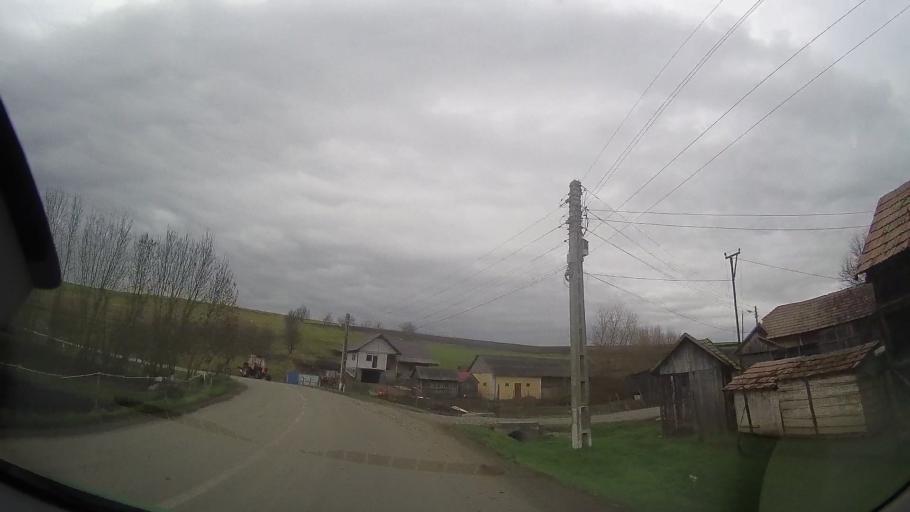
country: RO
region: Mures
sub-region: Comuna Craesti
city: Craiesti
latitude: 46.7714
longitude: 24.4246
